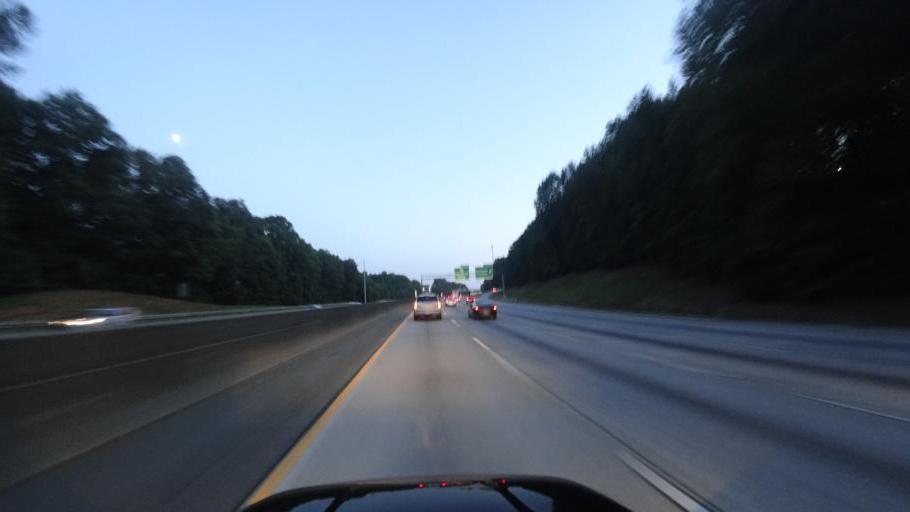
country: US
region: Georgia
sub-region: DeKalb County
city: Tucker
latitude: 33.8557
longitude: -84.2466
